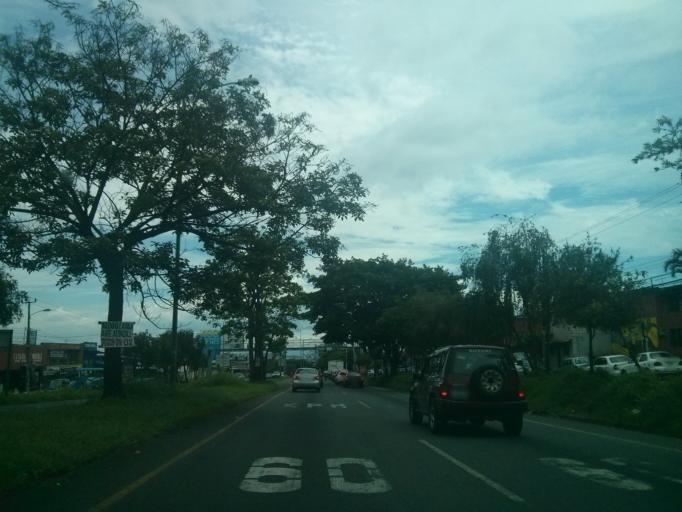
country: CR
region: San Jose
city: San Felipe
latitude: 9.9256
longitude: -84.1118
